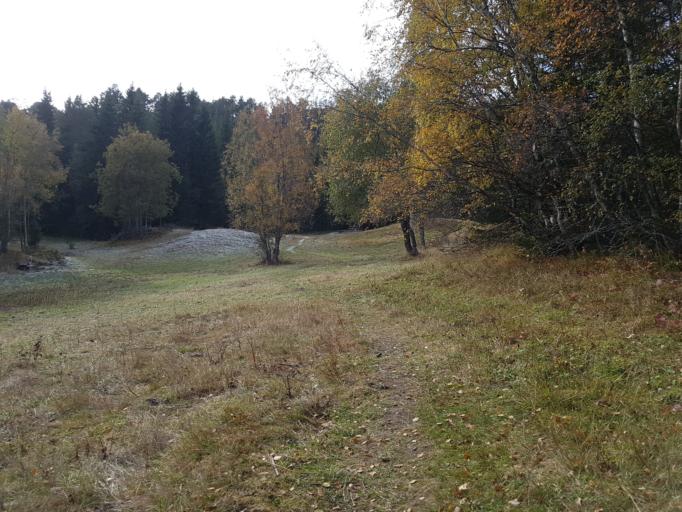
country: NO
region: Sor-Trondelag
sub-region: Trondheim
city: Trondheim
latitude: 63.4466
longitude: 10.2796
